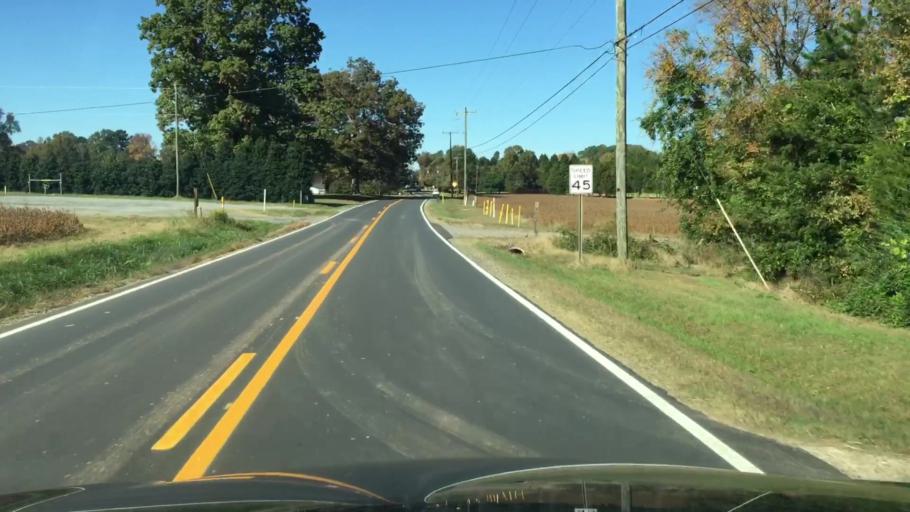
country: US
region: North Carolina
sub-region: Iredell County
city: Mooresville
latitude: 35.5762
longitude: -80.7803
